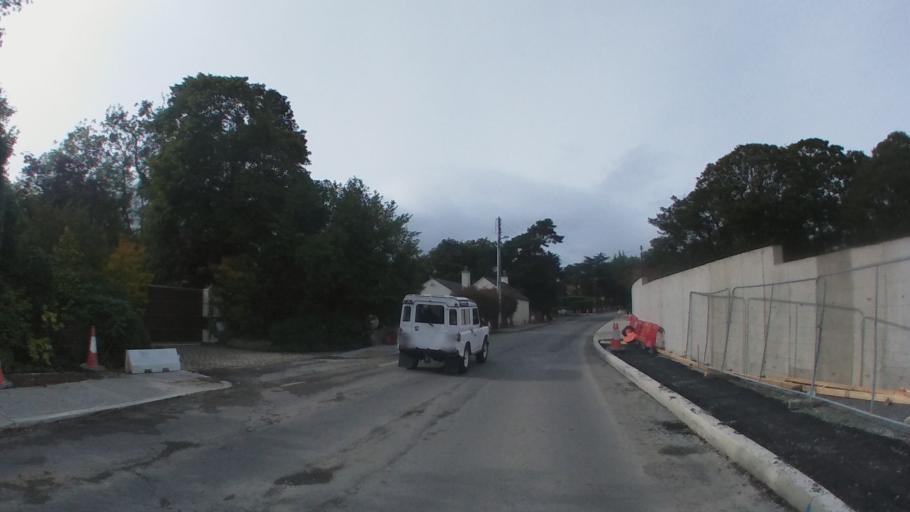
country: IE
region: Leinster
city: Foxrock
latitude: 53.2567
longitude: -6.1657
